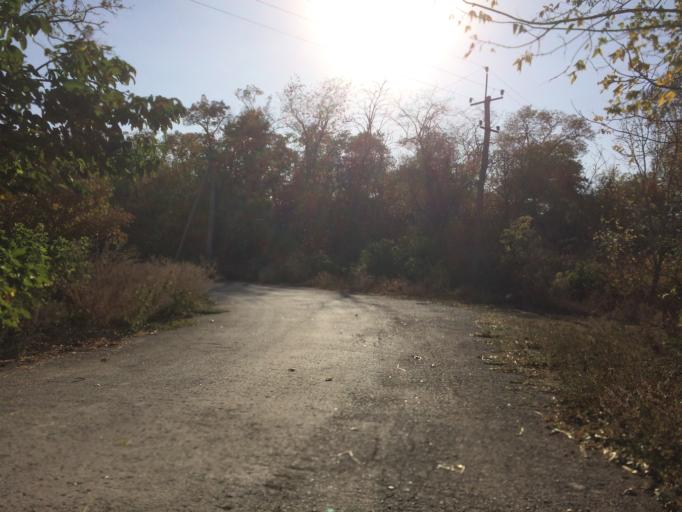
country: RU
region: Rostov
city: Gigant
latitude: 46.5214
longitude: 41.1937
